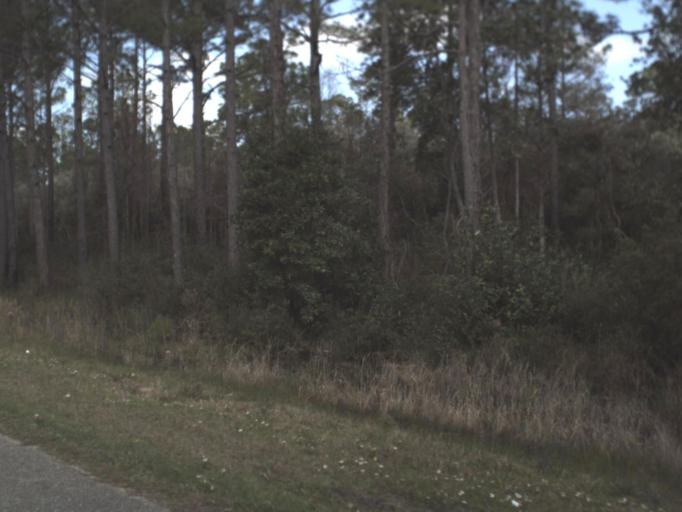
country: US
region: Florida
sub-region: Franklin County
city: Apalachicola
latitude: 29.7280
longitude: -85.1319
